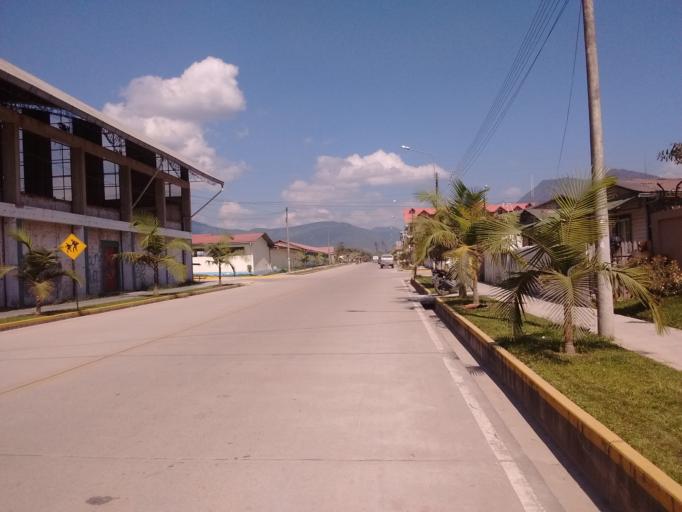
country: PE
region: Pasco
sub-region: Provincia de Oxapampa
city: Oxapampa
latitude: -10.5774
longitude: -75.4039
